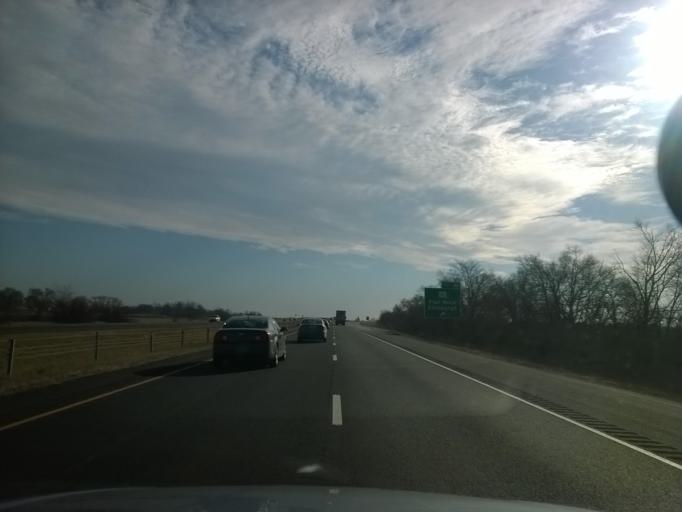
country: US
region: Indiana
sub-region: Johnson County
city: Edinburgh
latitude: 39.3693
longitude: -85.9427
